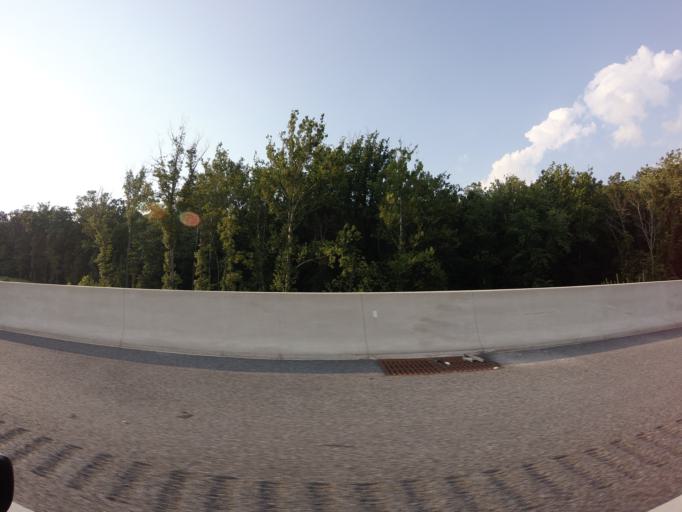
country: US
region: Maryland
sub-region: Prince George's County
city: Calverton
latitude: 39.0737
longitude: -76.9299
